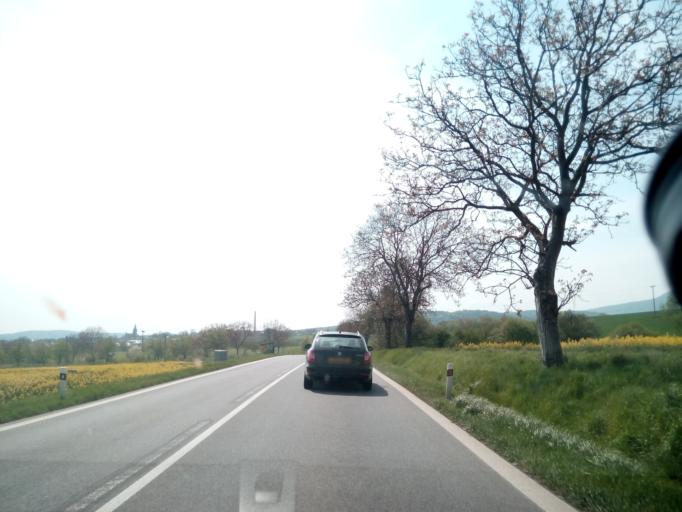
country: SK
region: Presovsky
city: Giraltovce
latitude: 49.0195
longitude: 21.5322
